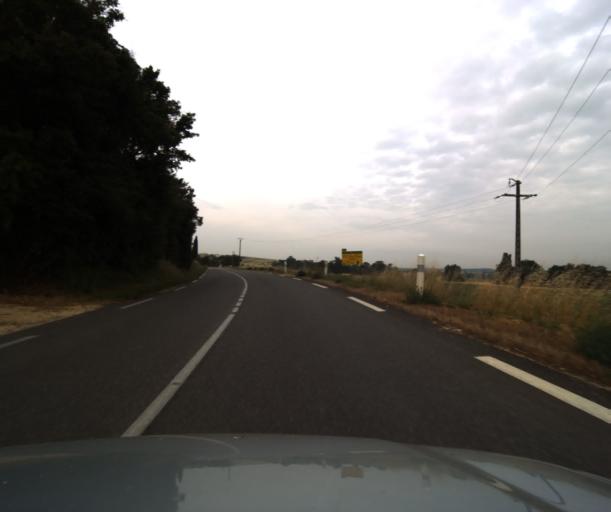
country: FR
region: Midi-Pyrenees
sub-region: Departement du Gers
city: Aubiet
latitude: 43.6671
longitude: 0.7988
